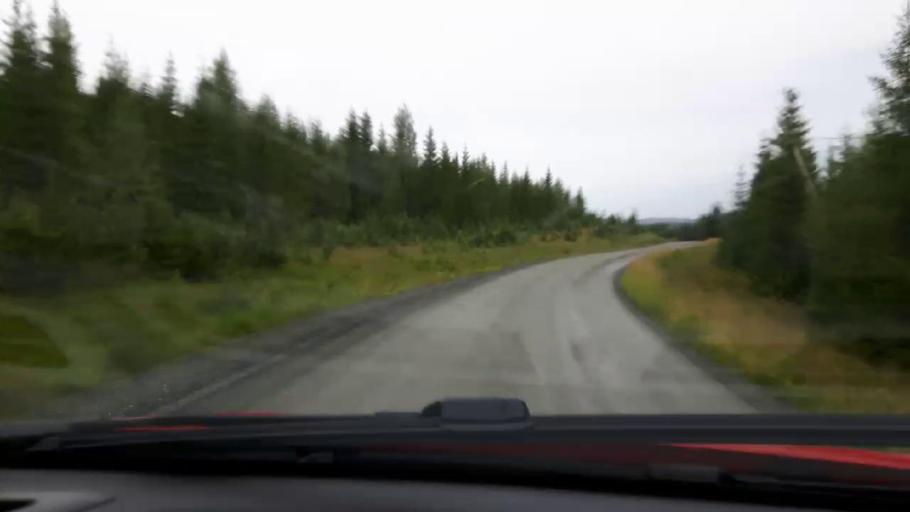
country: SE
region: Jaemtland
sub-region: Are Kommun
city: Are
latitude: 63.4230
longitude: 12.8199
